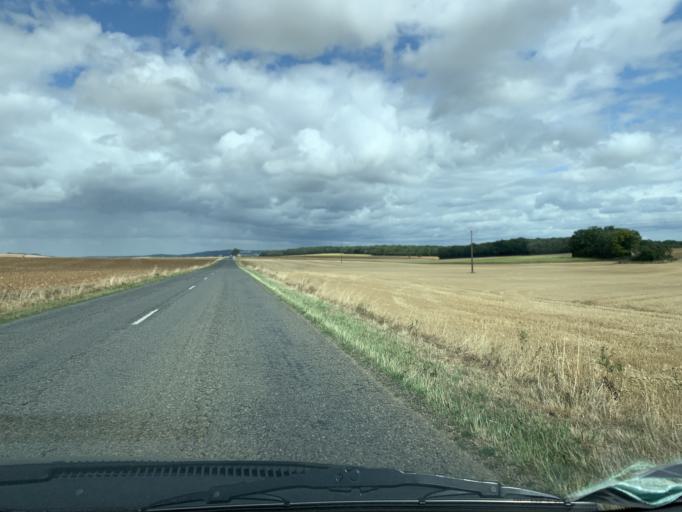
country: FR
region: Bourgogne
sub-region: Departement de la Nievre
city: Clamecy
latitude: 47.4172
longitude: 3.4618
